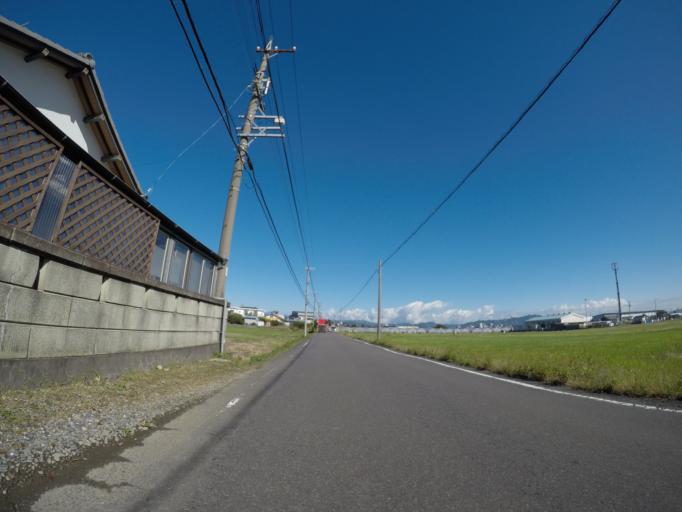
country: JP
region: Shizuoka
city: Fujieda
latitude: 34.8305
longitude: 138.2390
